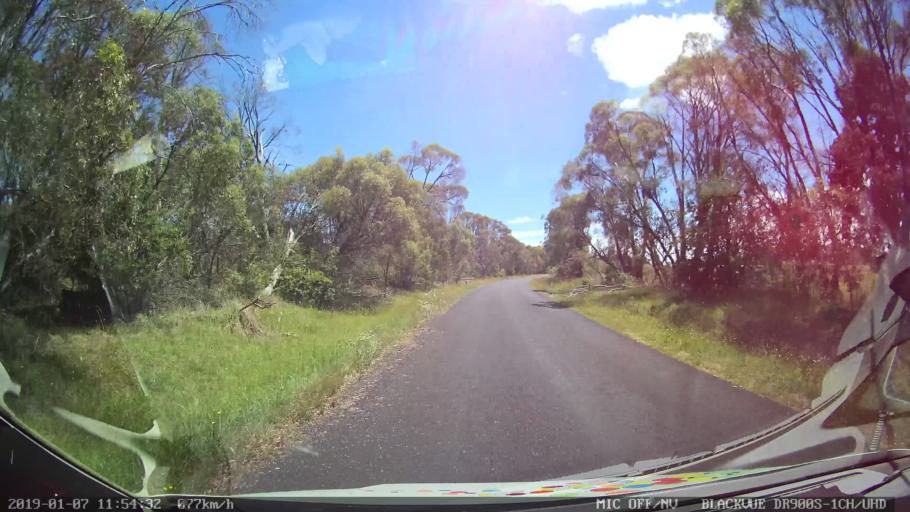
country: AU
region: New South Wales
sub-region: Guyra
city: Guyra
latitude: -30.2950
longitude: 151.6644
